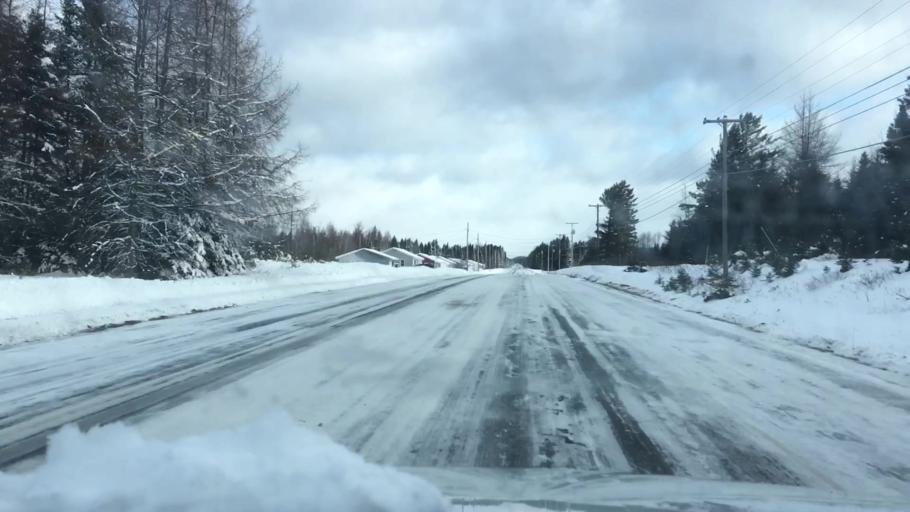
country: US
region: Maine
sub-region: Aroostook County
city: Madawaska
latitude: 47.0088
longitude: -68.0208
